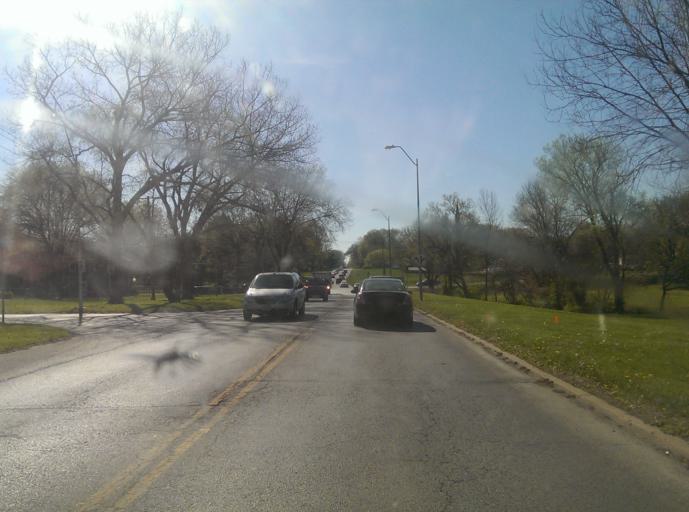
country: US
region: Kansas
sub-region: Johnson County
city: Leawood
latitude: 38.9263
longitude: -94.5910
